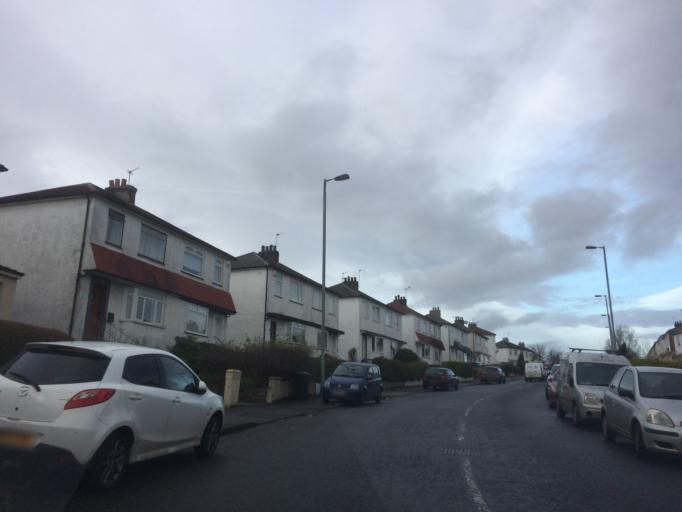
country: GB
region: Scotland
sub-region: East Renfrewshire
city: Giffnock
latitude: 55.8062
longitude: -4.3093
